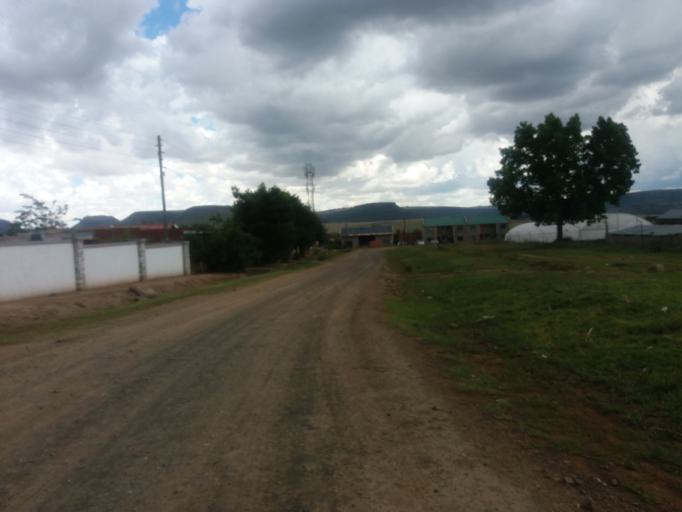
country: LS
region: Maseru
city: Maseru
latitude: -29.3003
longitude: 27.4971
